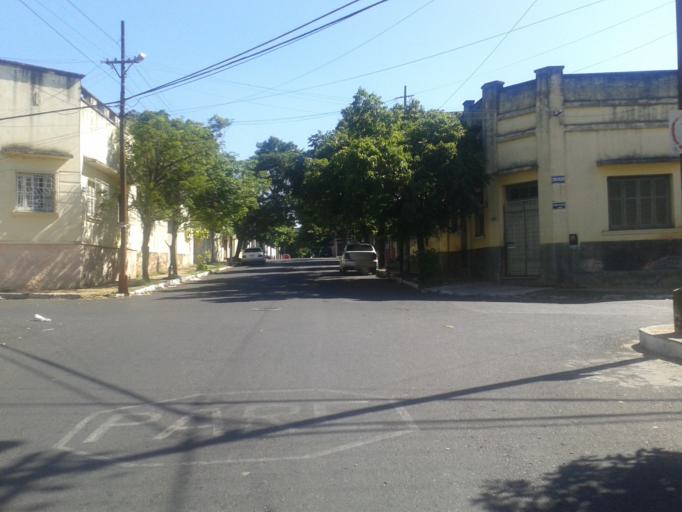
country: PY
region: Asuncion
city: Asuncion
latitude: -25.2929
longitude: -57.6371
